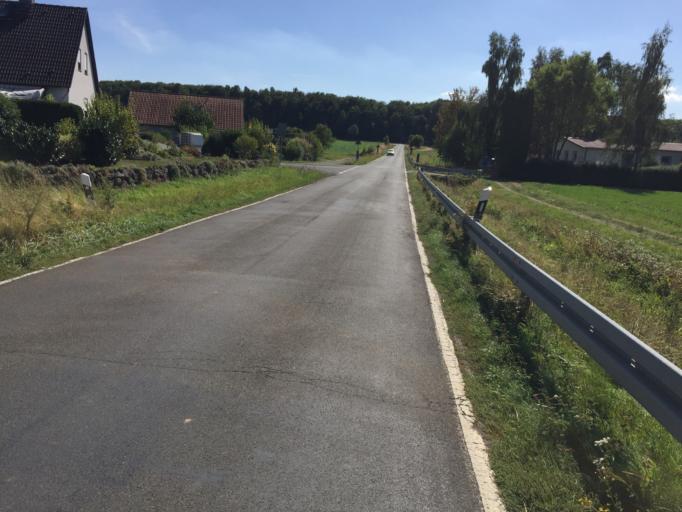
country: DE
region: Hesse
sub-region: Regierungsbezirk Giessen
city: Reiskirchen
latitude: 50.5922
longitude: 8.8743
